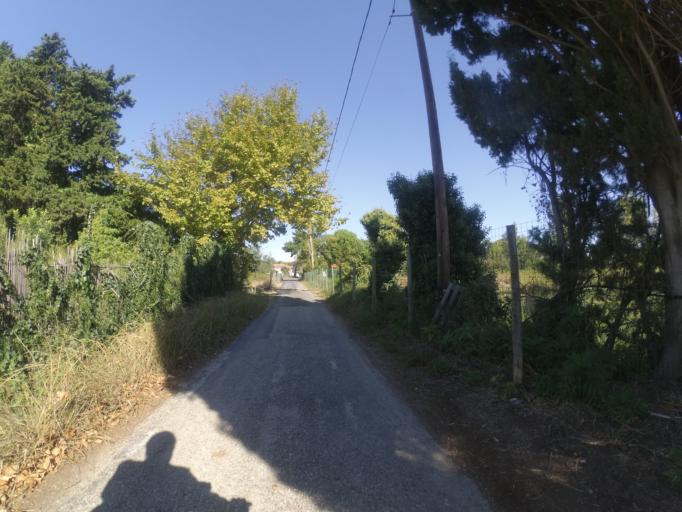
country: FR
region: Languedoc-Roussillon
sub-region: Departement des Pyrenees-Orientales
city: Pezilla-la-Riviere
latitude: 42.6891
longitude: 2.7677
